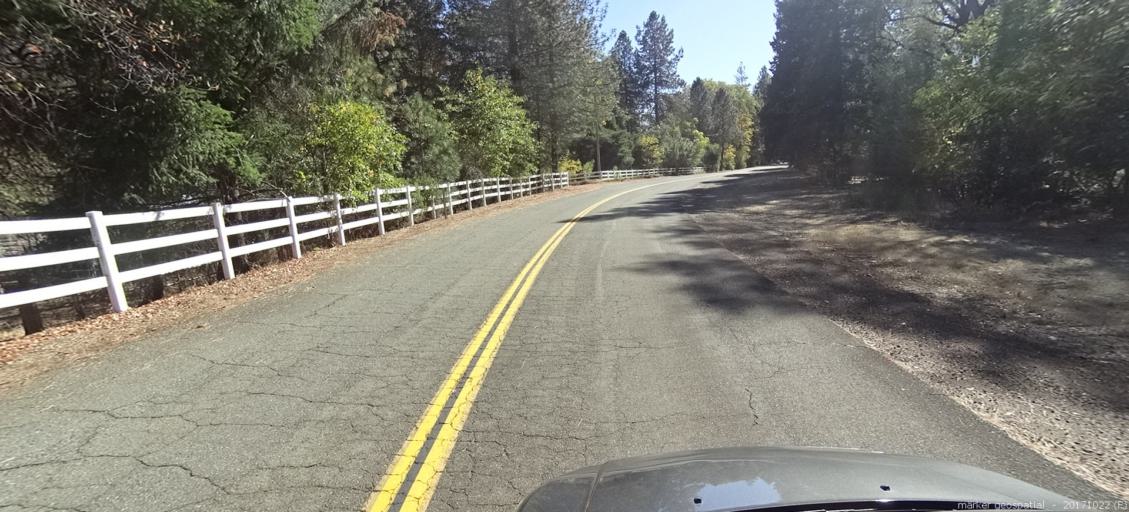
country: US
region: California
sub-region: Shasta County
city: Central Valley (historical)
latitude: 40.9135
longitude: -122.3835
